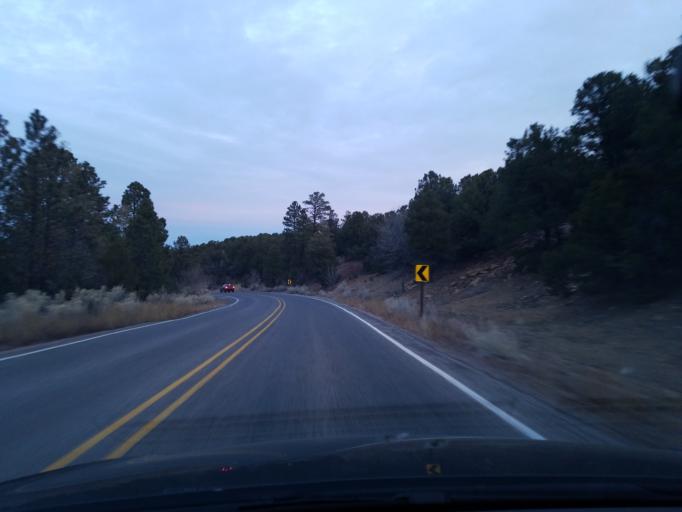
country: US
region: New Mexico
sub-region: Santa Fe County
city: Santa Fe
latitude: 35.7209
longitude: -105.8899
